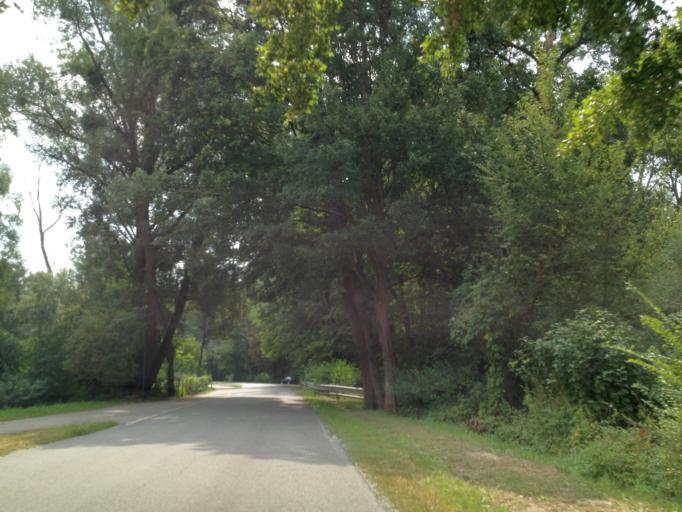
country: AT
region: Lower Austria
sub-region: Politischer Bezirk Ganserndorf
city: Orth an der Donau
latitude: 48.1298
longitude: 16.7081
